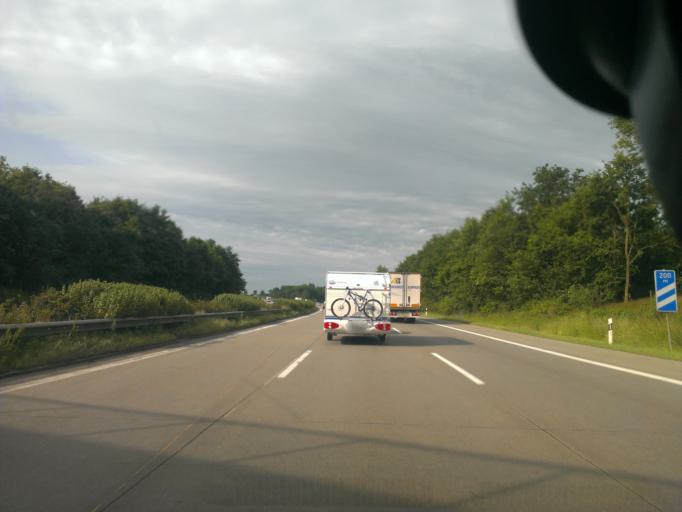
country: DE
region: Schleswig-Holstein
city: Braak
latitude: 53.6209
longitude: 10.2364
